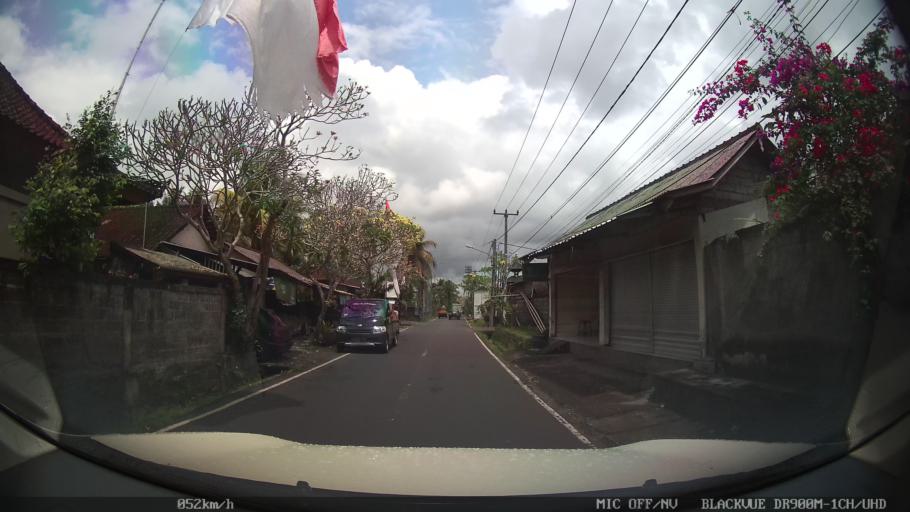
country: ID
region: Bali
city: Banjar Pekenjelodan
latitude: -8.5600
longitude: 115.1790
